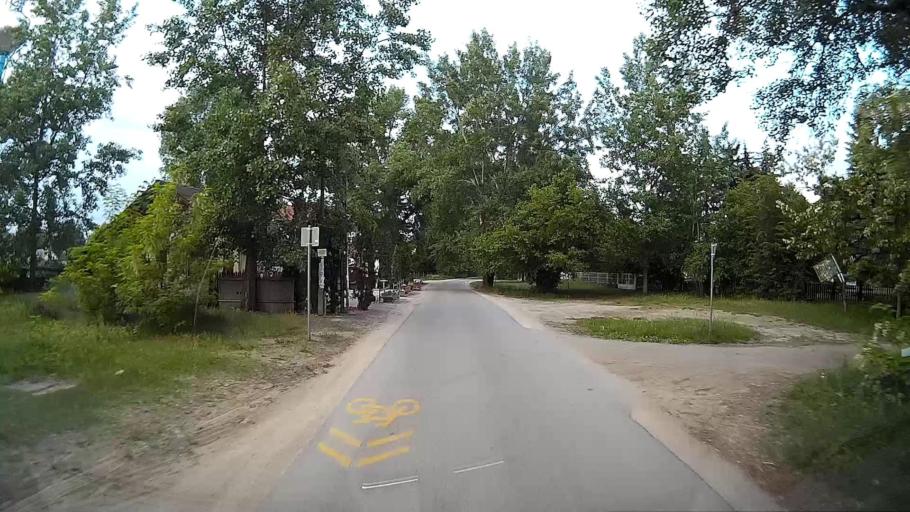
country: HU
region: Pest
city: God
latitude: 47.6709
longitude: 19.1117
